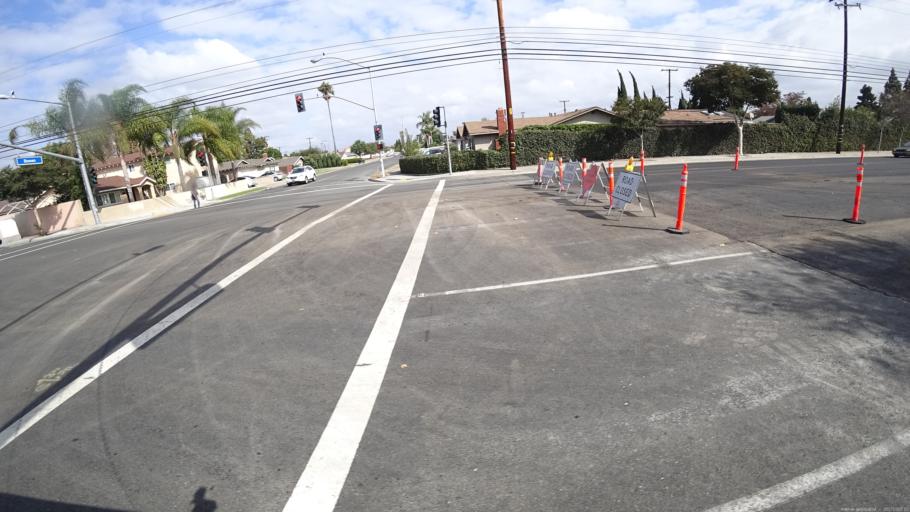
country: US
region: California
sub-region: Orange County
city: Garden Grove
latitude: 33.7595
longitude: -117.9475
